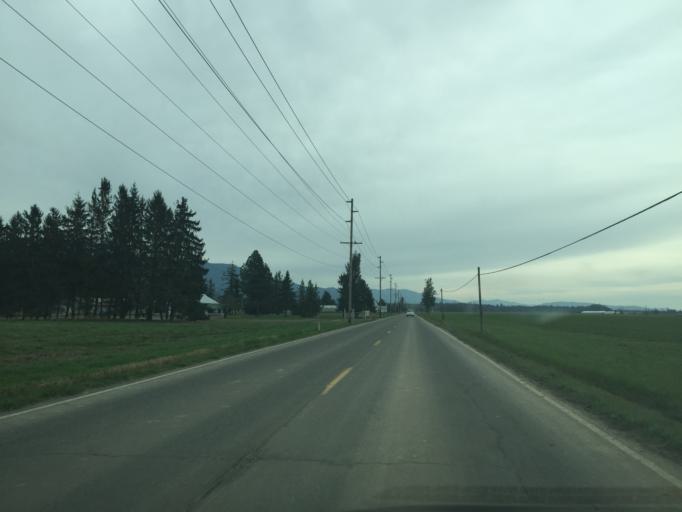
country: US
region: Washington
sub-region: Whatcom County
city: Sumas
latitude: 48.9845
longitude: -122.2866
